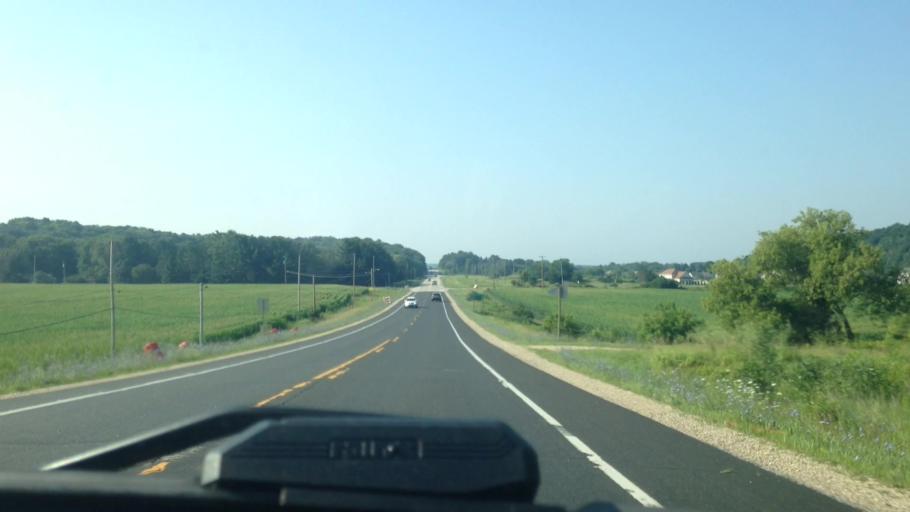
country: US
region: Wisconsin
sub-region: Waukesha County
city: Merton
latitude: 43.2110
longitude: -88.2617
